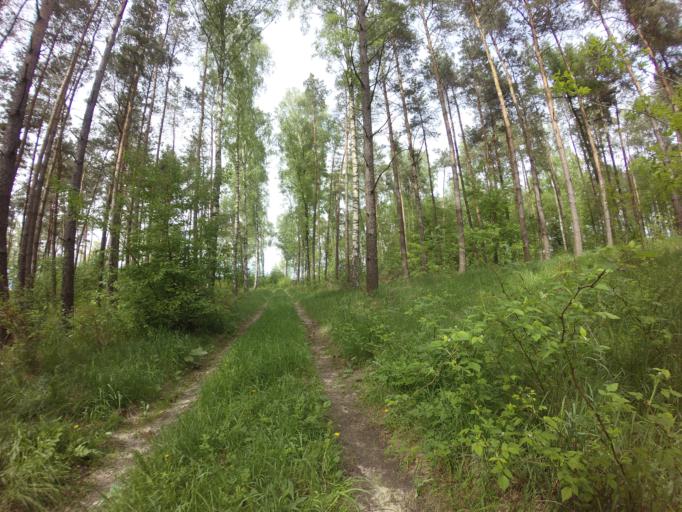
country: PL
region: West Pomeranian Voivodeship
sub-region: Powiat choszczenski
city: Recz
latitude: 53.1554
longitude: 15.5855
